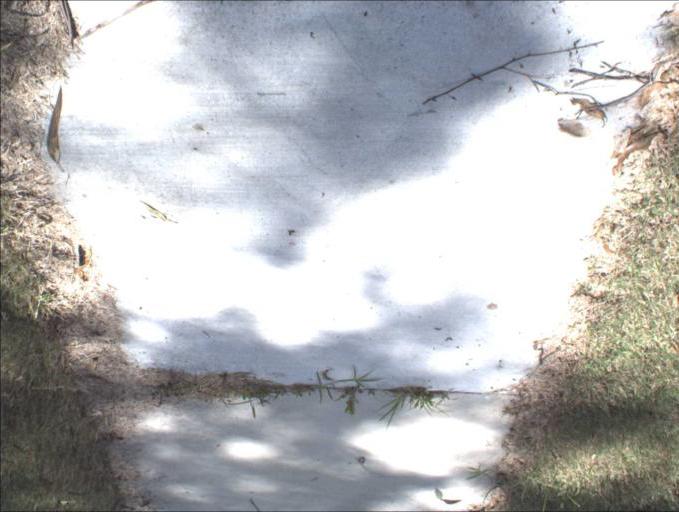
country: AU
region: Queensland
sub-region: Logan
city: Cedar Vale
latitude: -27.8445
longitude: 153.0216
